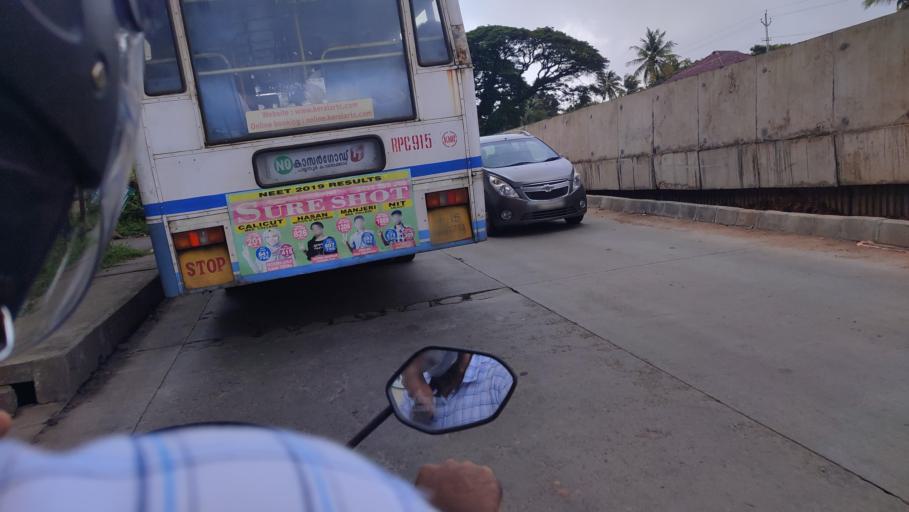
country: IN
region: Kerala
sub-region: Kasaragod District
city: Nileshwar
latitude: 12.2434
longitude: 75.1429
